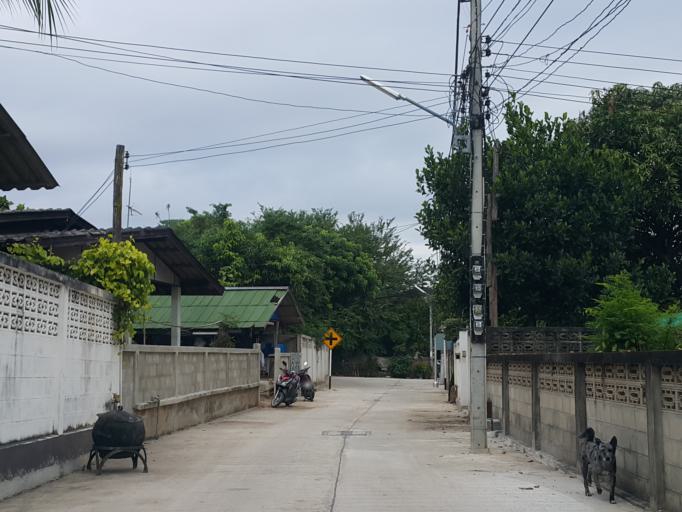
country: TH
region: Lampang
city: Lampang
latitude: 18.2972
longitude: 99.5115
